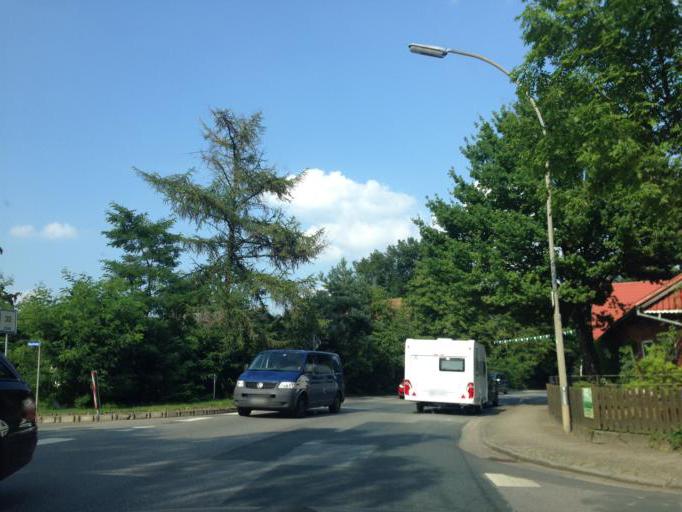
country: DE
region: Lower Saxony
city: Uetze
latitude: 52.4561
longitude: 10.2653
